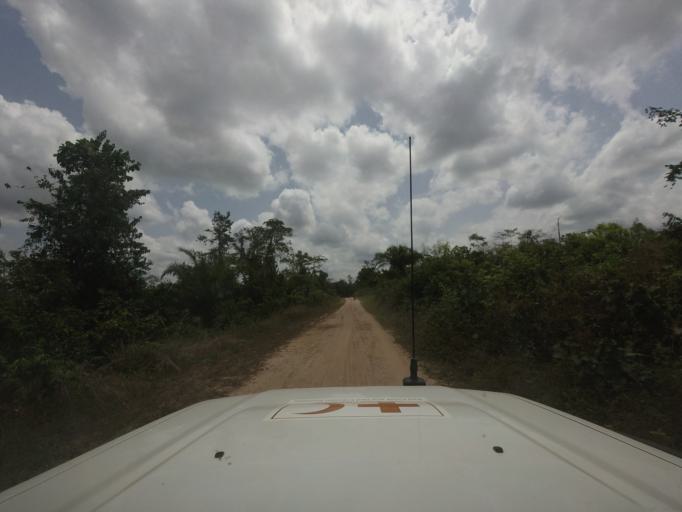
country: GN
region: Nzerekore
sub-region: Yomou
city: Yomou
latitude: 7.2616
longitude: -9.1905
